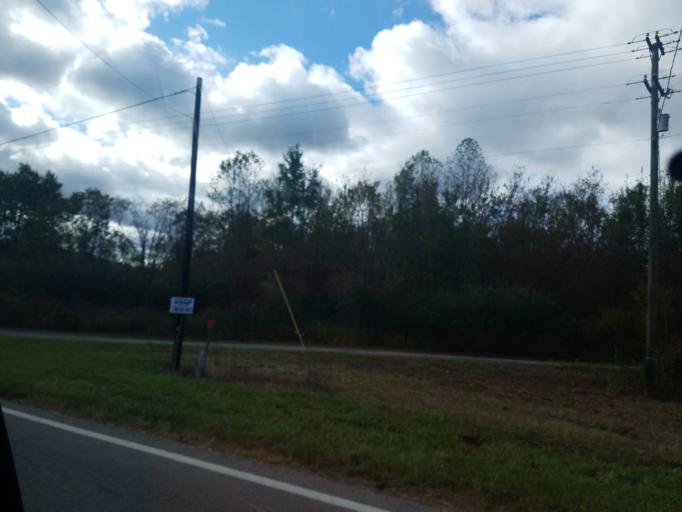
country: US
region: Ohio
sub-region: Vinton County
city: McArthur
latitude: 39.1917
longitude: -82.4757
